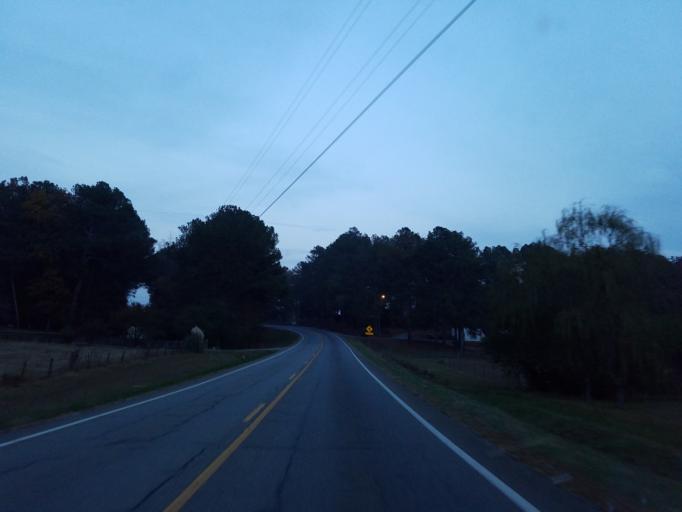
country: US
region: Georgia
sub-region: Pickens County
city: Jasper
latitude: 34.5106
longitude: -84.5498
